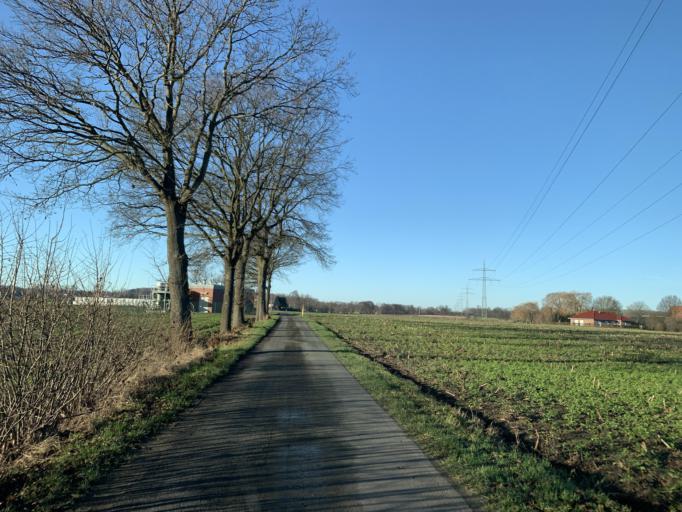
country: DE
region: North Rhine-Westphalia
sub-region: Regierungsbezirk Munster
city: Dulmen
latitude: 51.8512
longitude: 7.3084
